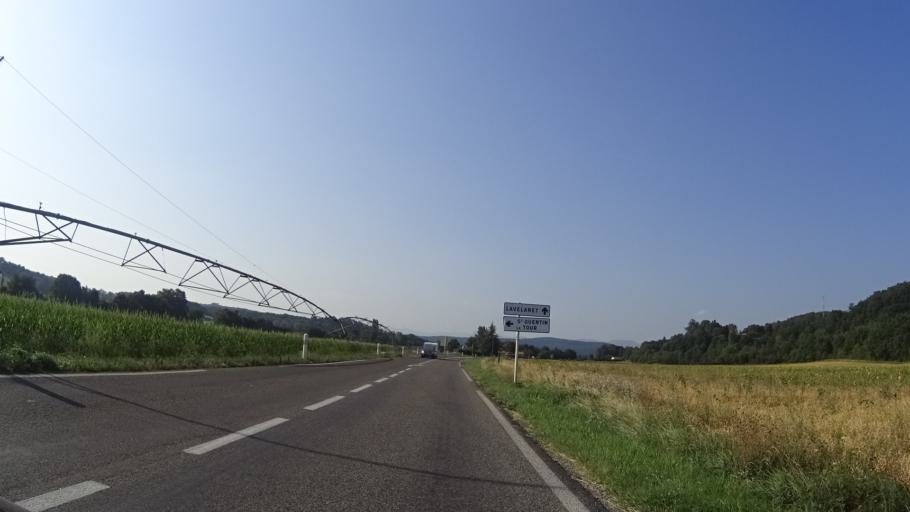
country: FR
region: Midi-Pyrenees
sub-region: Departement de l'Ariege
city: Mirepoix
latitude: 43.0405
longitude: 1.8973
